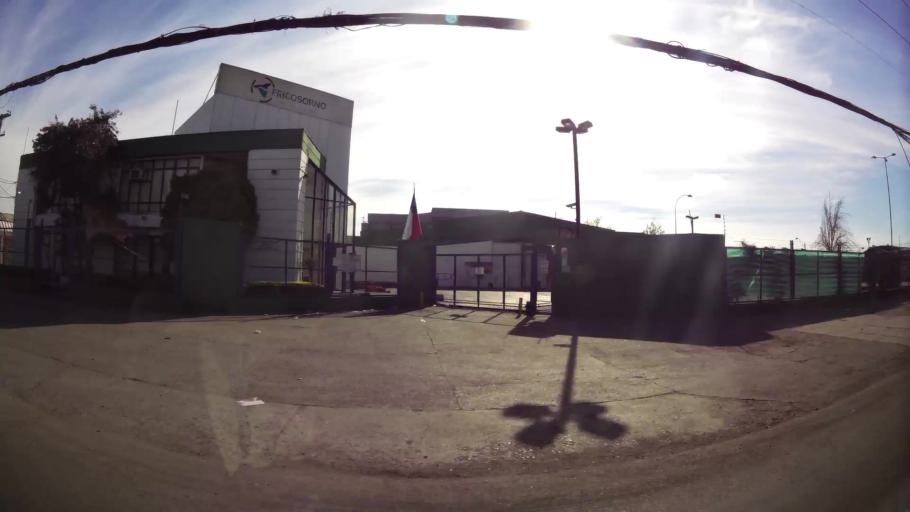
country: CL
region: Santiago Metropolitan
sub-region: Provincia de Santiago
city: Santiago
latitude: -33.4595
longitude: -70.6809
